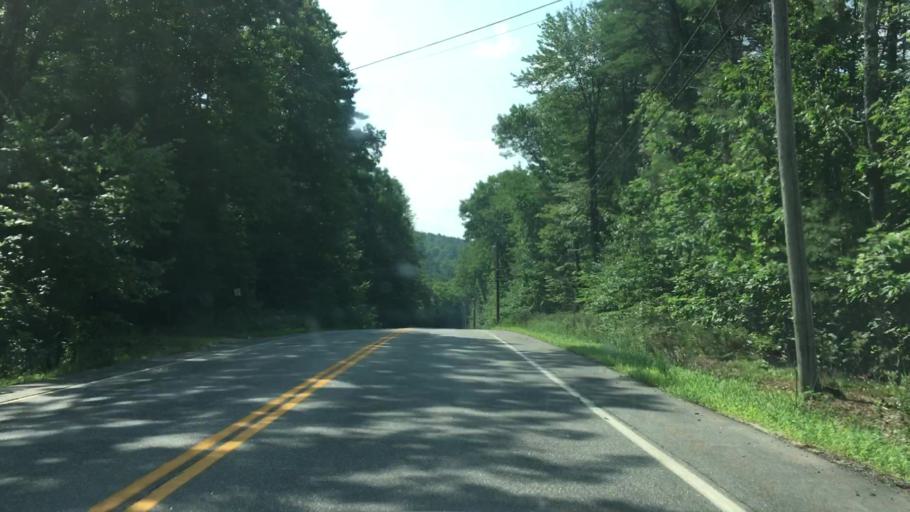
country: US
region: Maine
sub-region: Cumberland County
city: Raymond
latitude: 43.9318
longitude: -70.4384
